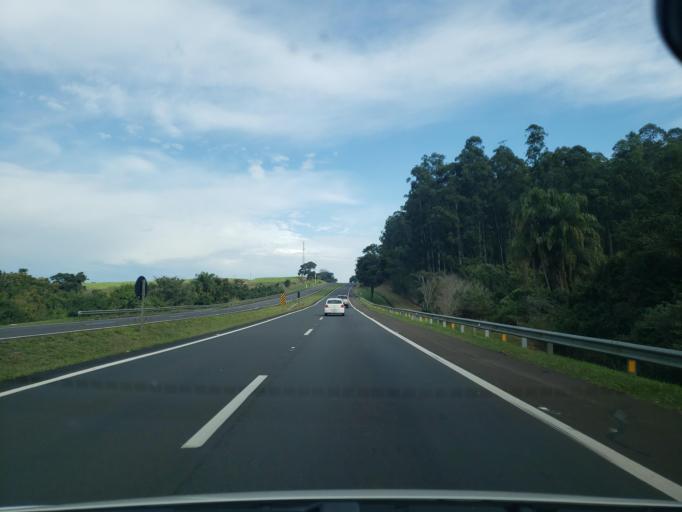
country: BR
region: Sao Paulo
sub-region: Itirapina
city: Itirapina
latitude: -22.2751
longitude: -47.9668
